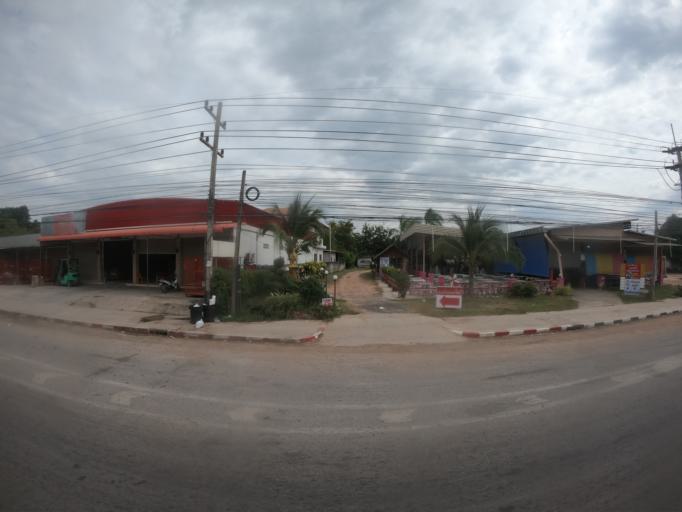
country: TH
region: Maha Sarakham
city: Maha Sarakham
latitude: 16.2293
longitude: 103.2712
